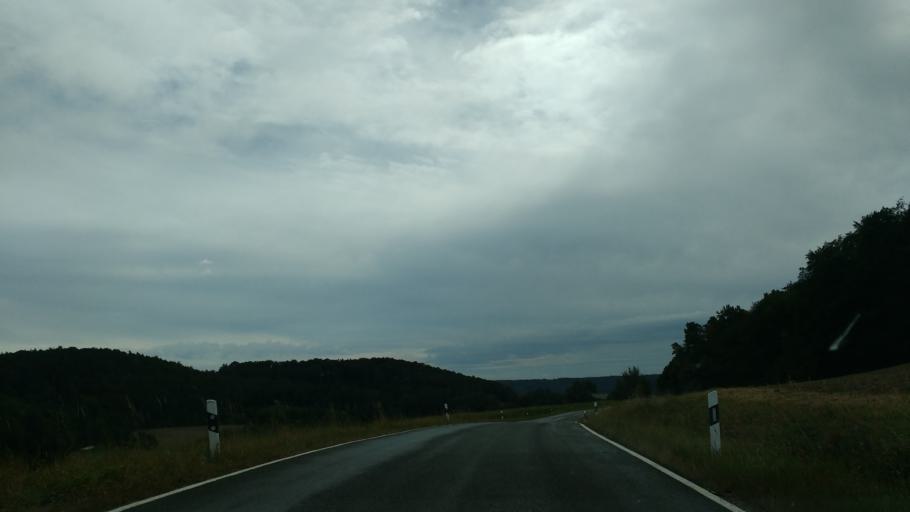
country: DE
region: Bavaria
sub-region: Regierungsbezirk Unterfranken
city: Geiselwind
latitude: 49.7939
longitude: 10.4960
